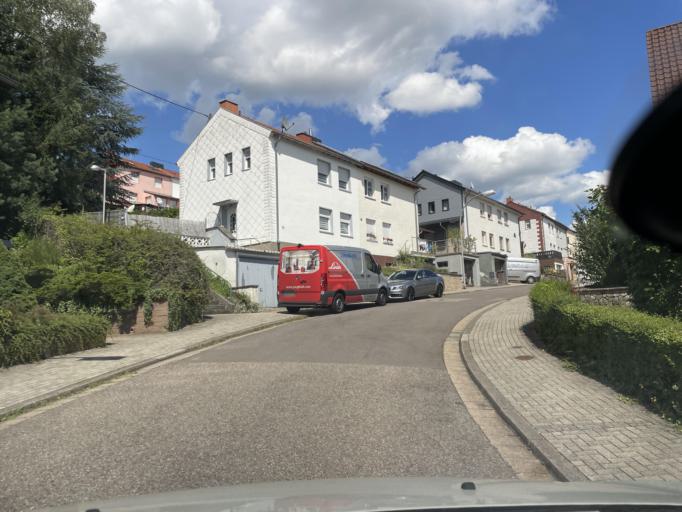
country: DE
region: Saarland
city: Sulzbach
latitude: 49.2718
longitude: 7.0492
